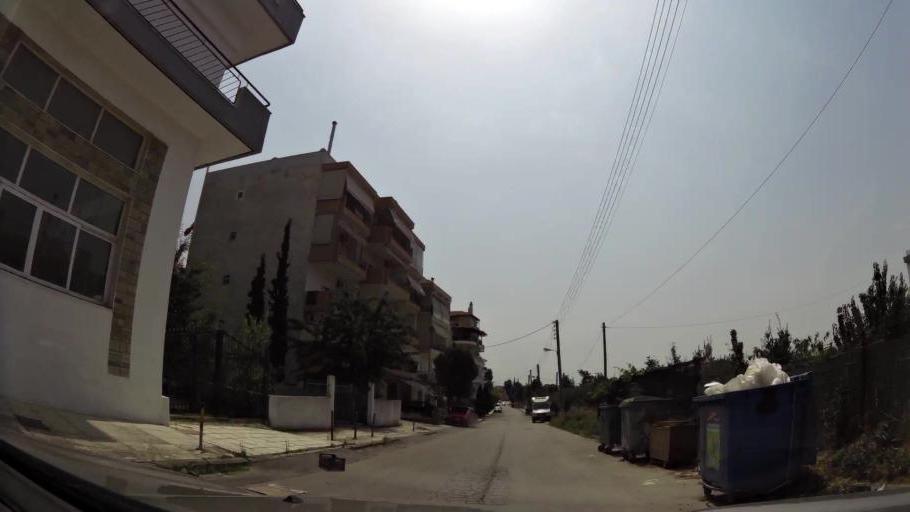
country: GR
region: Central Macedonia
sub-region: Nomos Thessalonikis
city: Diavata
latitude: 40.6920
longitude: 22.8562
